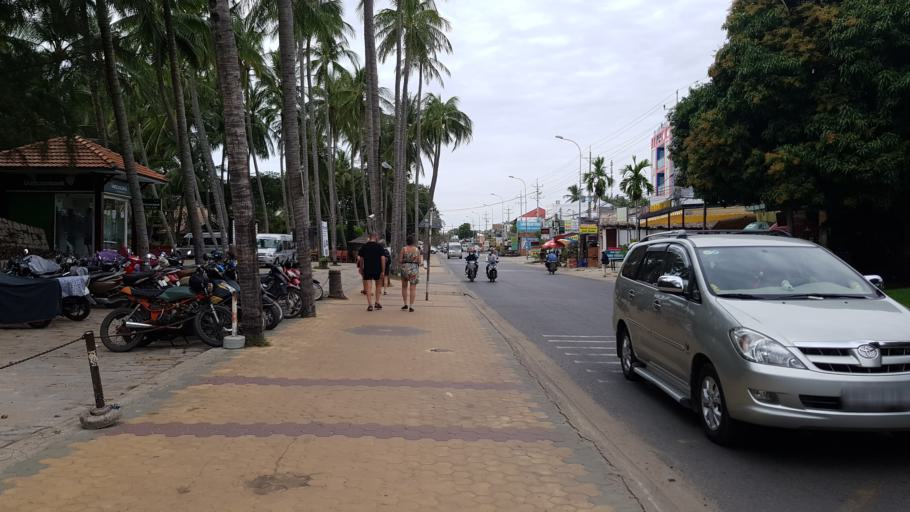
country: VN
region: Binh Thuan
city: Phan Thiet
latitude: 10.9485
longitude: 108.2042
